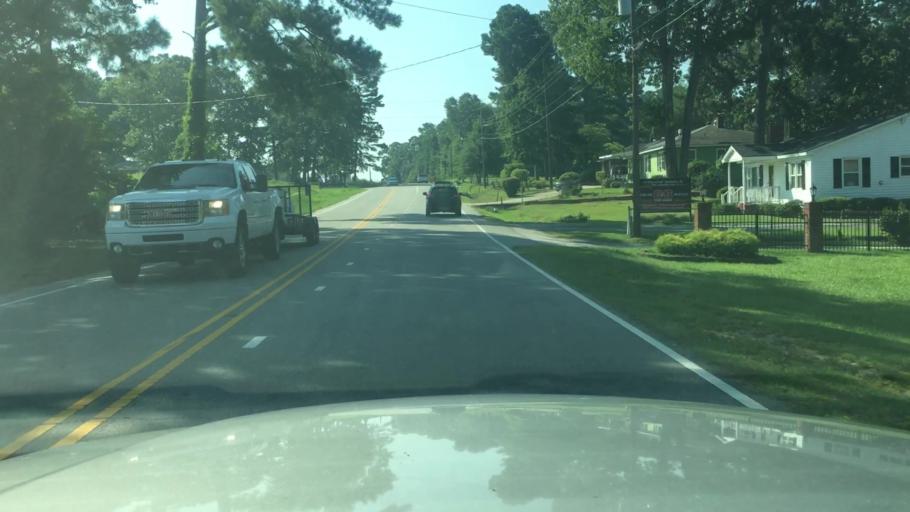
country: US
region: North Carolina
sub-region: Cumberland County
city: Fayetteville
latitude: 35.1211
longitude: -78.8852
